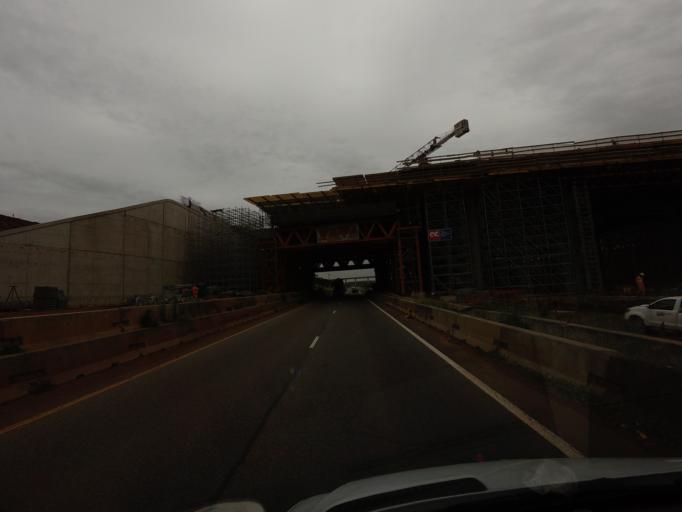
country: ZA
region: KwaZulu-Natal
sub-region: eThekwini Metropolitan Municipality
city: Durban
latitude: -29.7148
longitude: 31.0639
